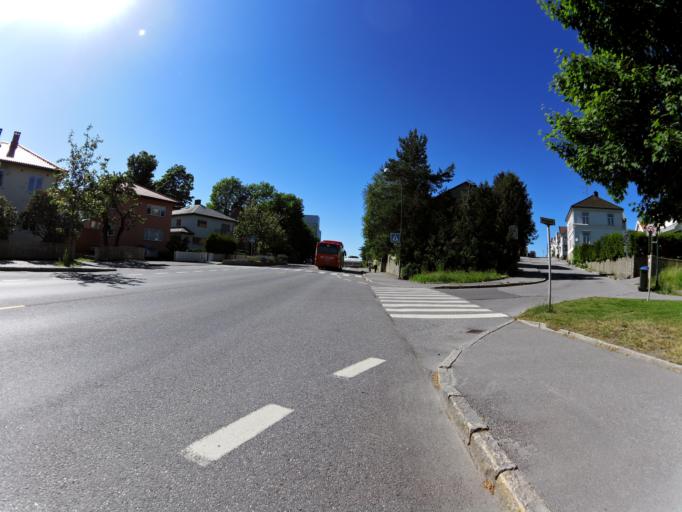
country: NO
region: Ostfold
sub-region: Fredrikstad
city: Fredrikstad
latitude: 59.2108
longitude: 10.9431
